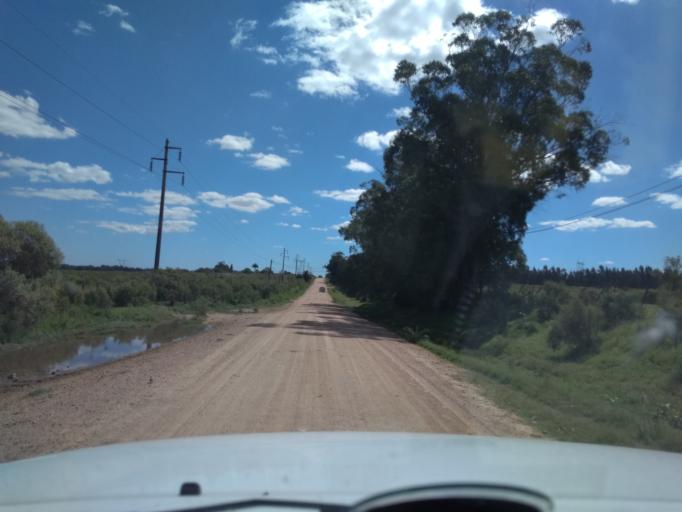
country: UY
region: Canelones
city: Pando
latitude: -34.6968
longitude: -55.9801
